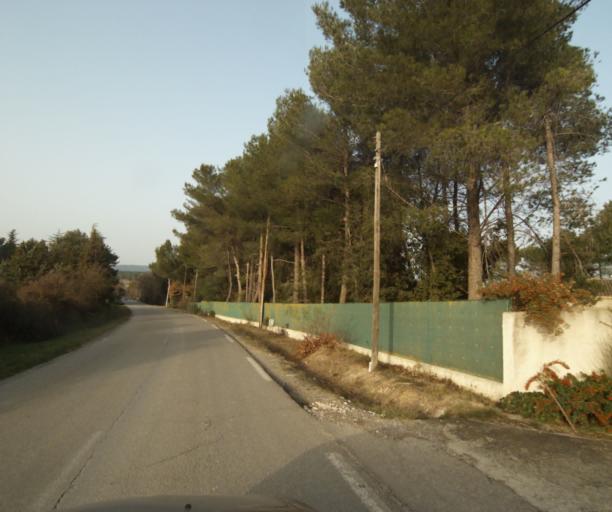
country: FR
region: Provence-Alpes-Cote d'Azur
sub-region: Departement des Bouches-du-Rhone
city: Eguilles
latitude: 43.5797
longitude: 5.3652
